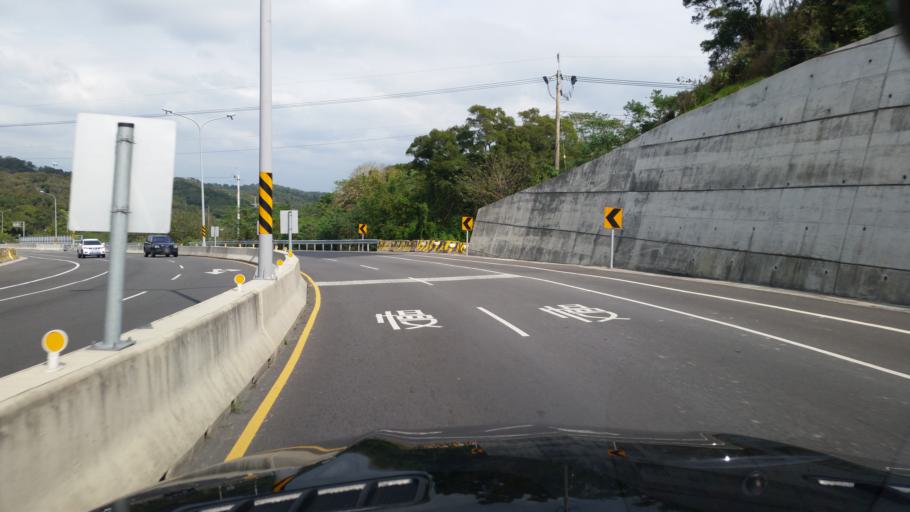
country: TW
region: Taiwan
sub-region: Miaoli
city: Miaoli
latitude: 24.6265
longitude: 120.8525
